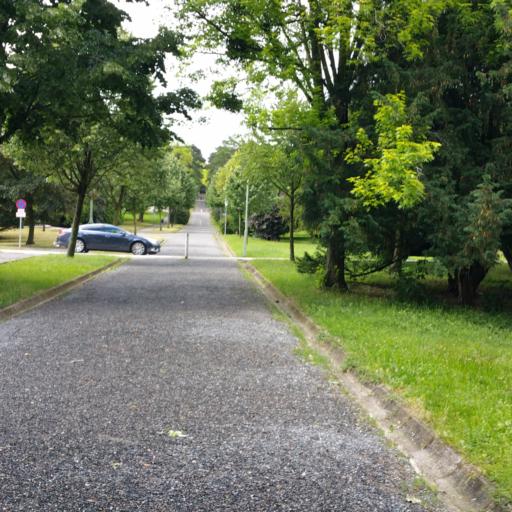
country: AT
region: Lower Austria
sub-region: Politischer Bezirk Modling
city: Perchtoldsdorf
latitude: 48.2077
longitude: 16.2808
